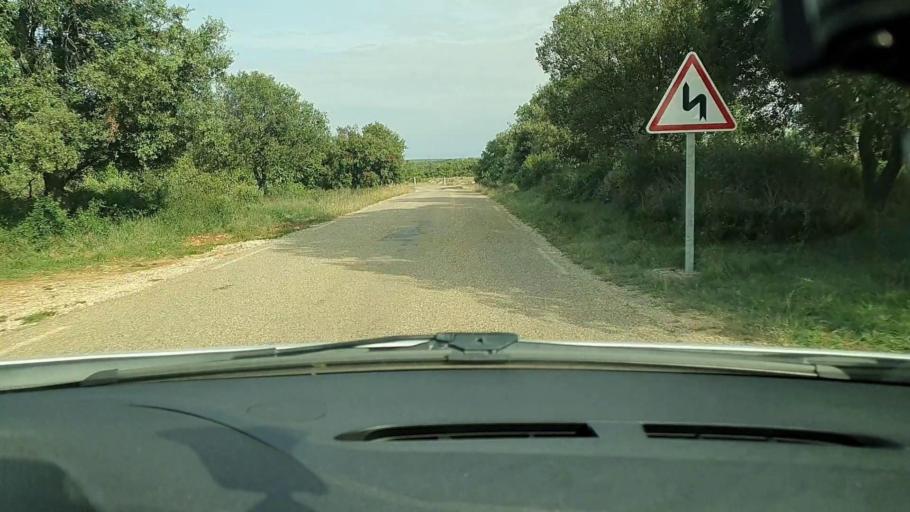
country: FR
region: Languedoc-Roussillon
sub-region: Departement du Gard
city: Saint-Quentin-la-Poterie
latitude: 44.1252
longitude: 4.4118
